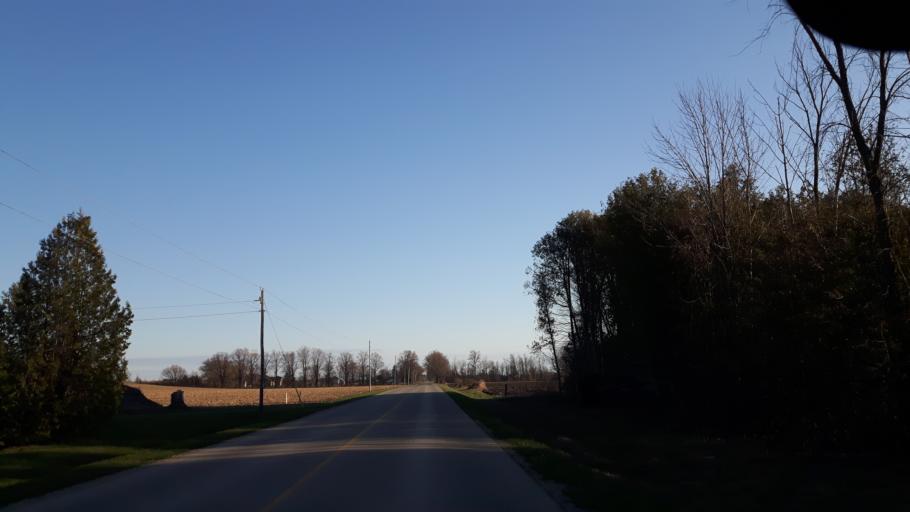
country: CA
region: Ontario
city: Goderich
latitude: 43.6843
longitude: -81.6848
